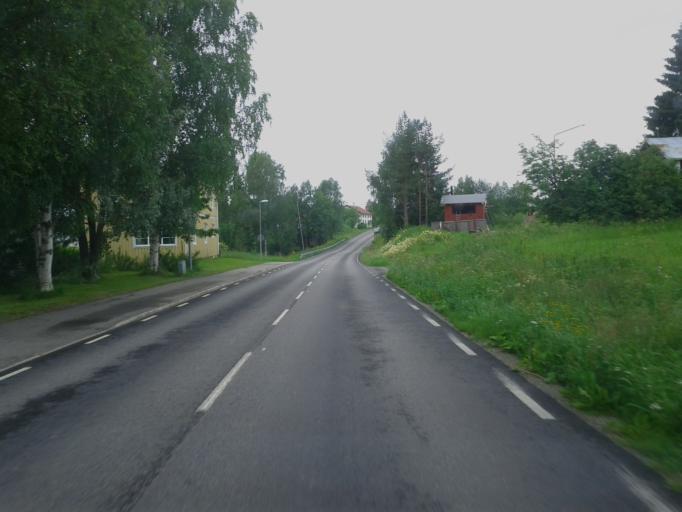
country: SE
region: Vaesterbotten
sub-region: Skelleftea Kommun
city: Viken
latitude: 64.8802
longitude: 20.7836
